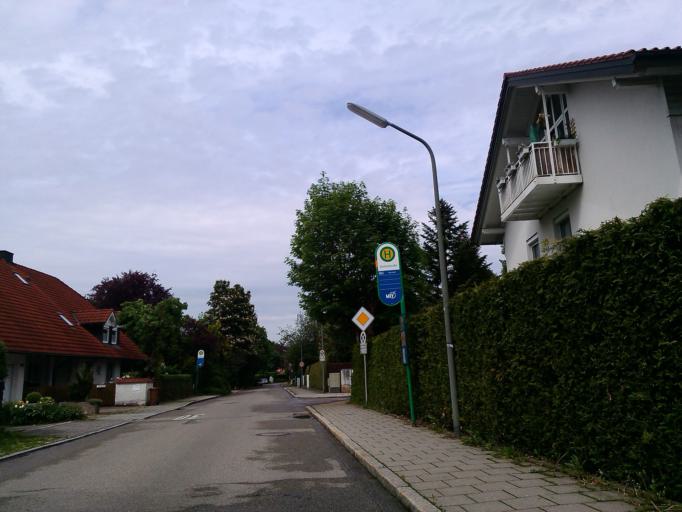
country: DE
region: Bavaria
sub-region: Upper Bavaria
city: Gauting
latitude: 48.0674
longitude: 11.3909
